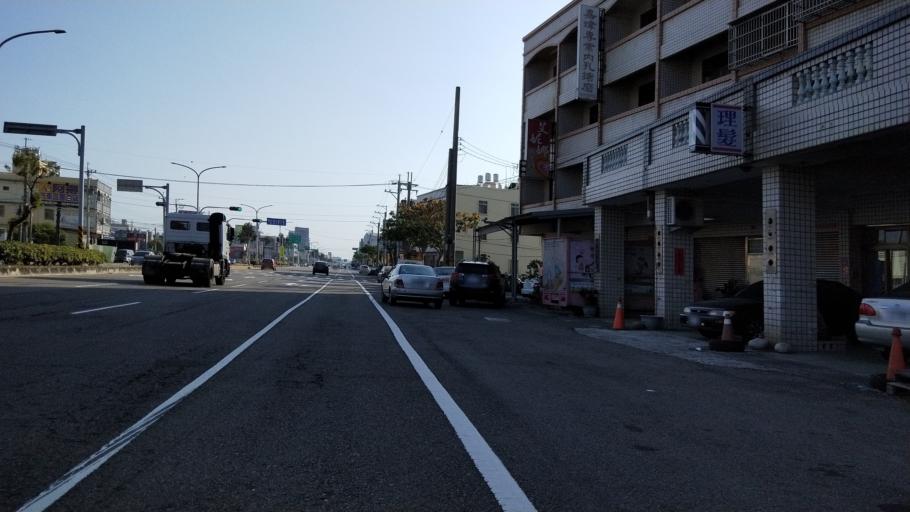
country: TW
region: Taiwan
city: Fengyuan
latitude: 24.2589
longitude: 120.5594
